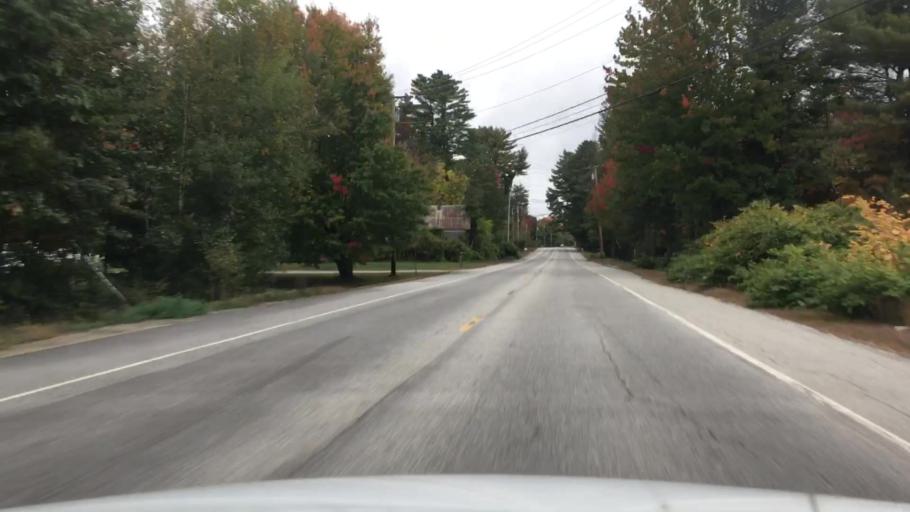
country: US
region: Maine
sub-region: Oxford County
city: Oxford
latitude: 44.1274
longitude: -70.4549
